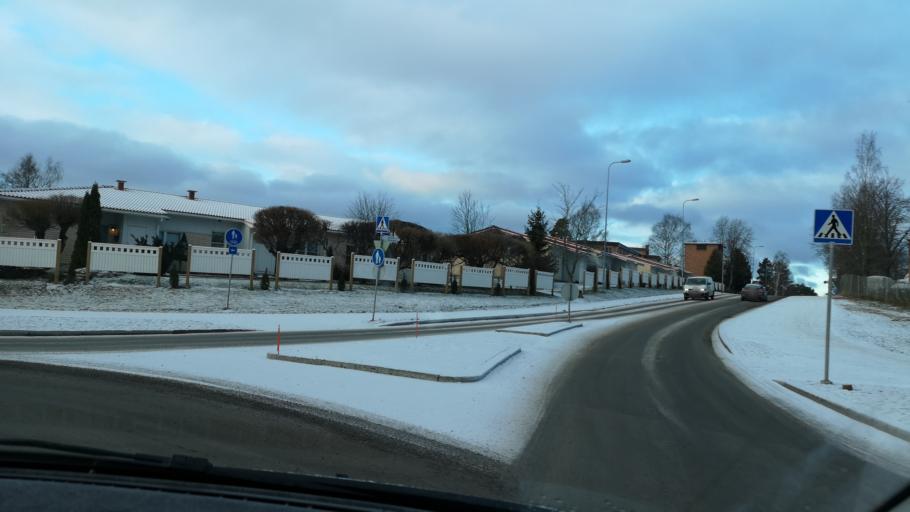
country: FI
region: Ostrobothnia
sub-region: Vaasa
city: Vaasa
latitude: 63.1161
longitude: 21.6182
